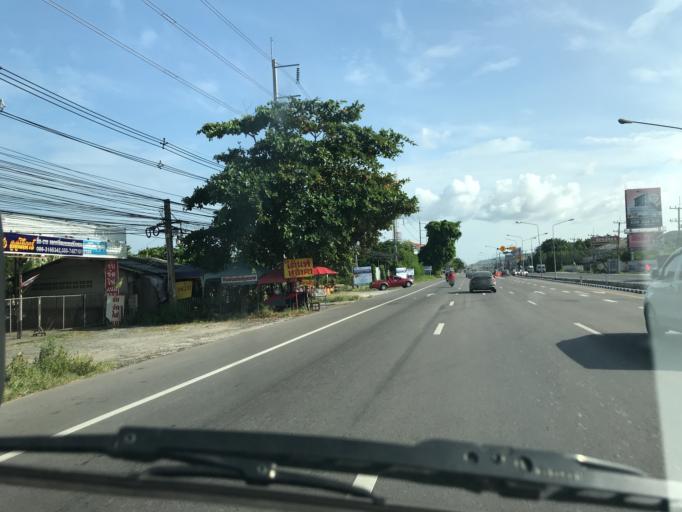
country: TH
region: Chon Buri
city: Bang Lamung
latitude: 13.0484
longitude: 100.9264
